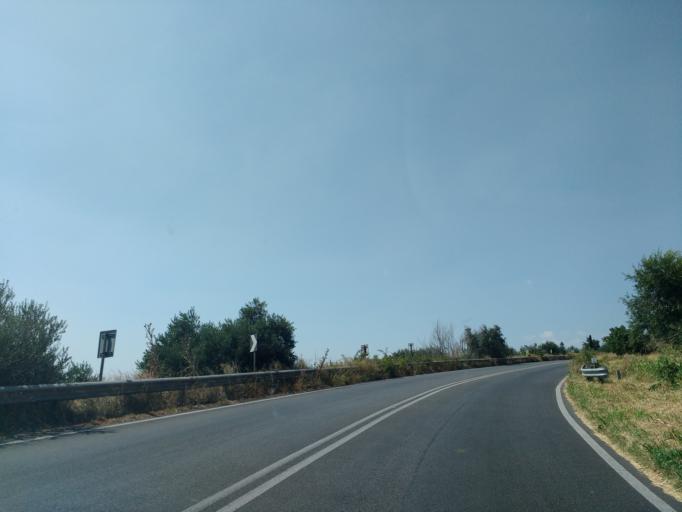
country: IT
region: Latium
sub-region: Citta metropolitana di Roma Capitale
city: Tivoli
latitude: 41.9493
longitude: 12.7915
